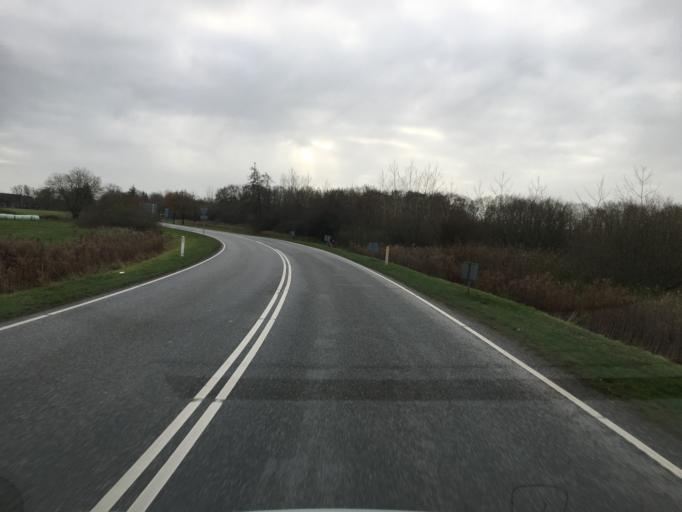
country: DK
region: South Denmark
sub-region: Tonder Kommune
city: Tonder
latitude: 54.9647
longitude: 8.8677
